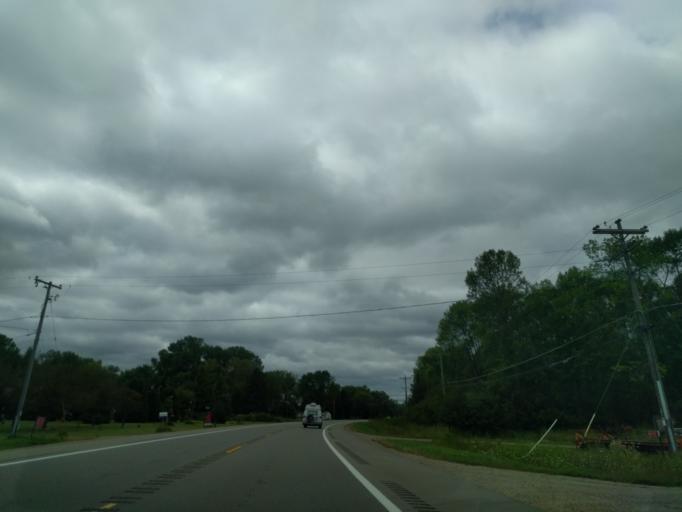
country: US
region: Michigan
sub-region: Menominee County
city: Menominee
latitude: 45.1735
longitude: -87.5735
